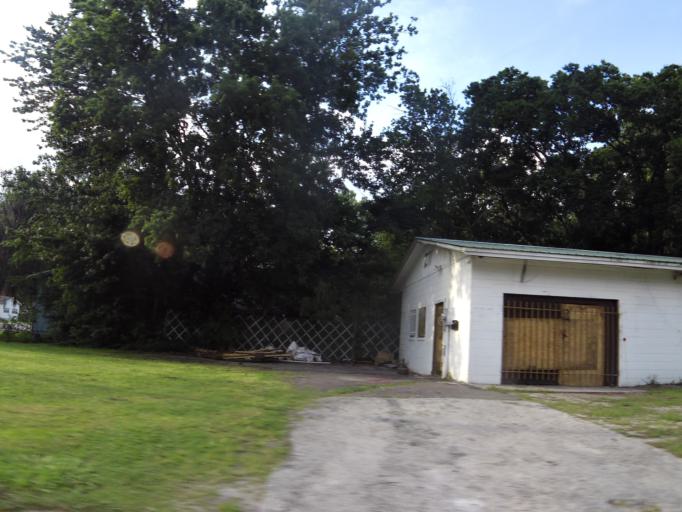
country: US
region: Florida
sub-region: Duval County
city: Jacksonville
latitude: 30.3202
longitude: -81.7516
